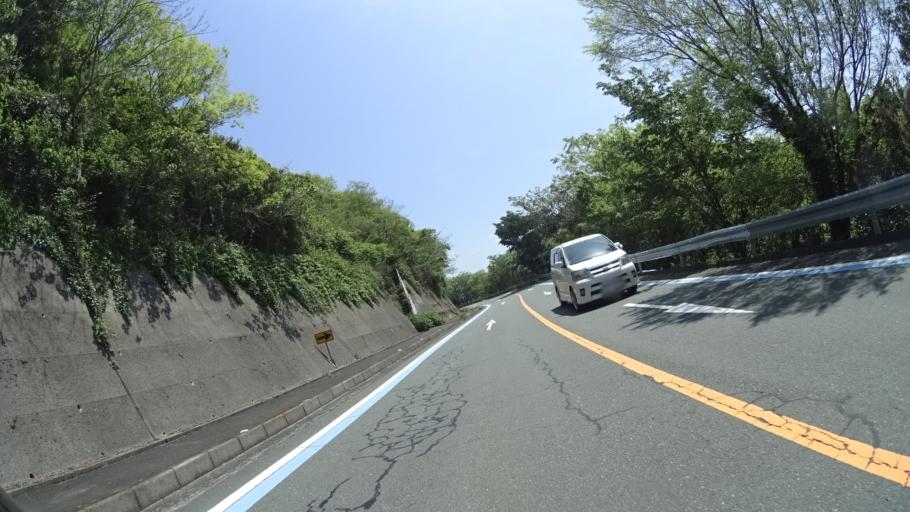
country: JP
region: Ehime
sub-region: Nishiuwa-gun
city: Ikata-cho
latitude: 33.4656
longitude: 132.2735
